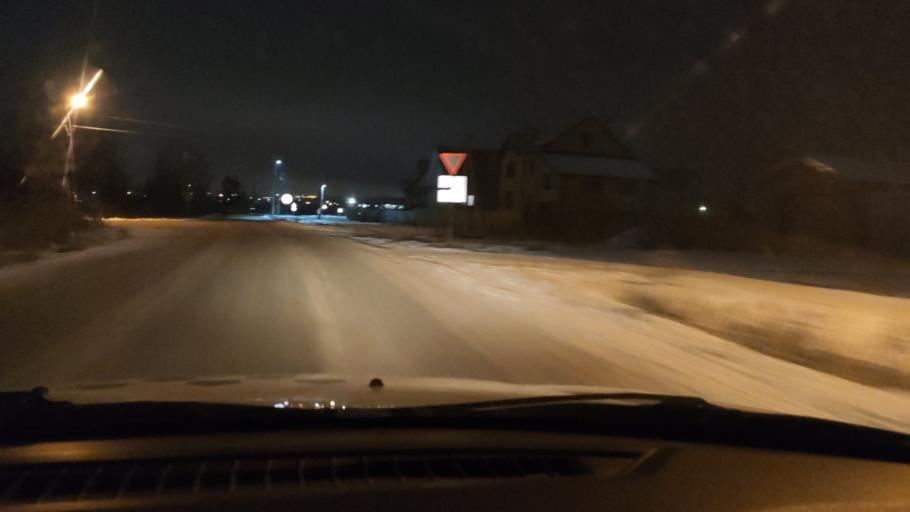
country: RU
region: Perm
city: Ferma
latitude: 57.8949
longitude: 56.3267
